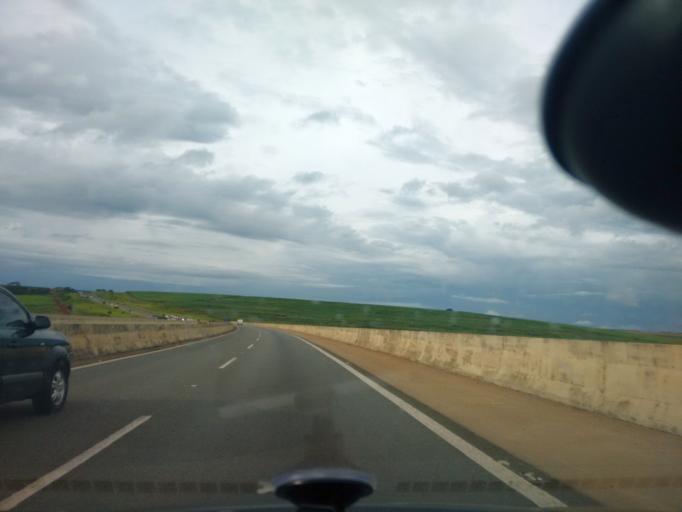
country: BR
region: Sao Paulo
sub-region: Cordeiropolis
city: Cordeiropolis
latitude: -22.5217
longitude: -47.4326
